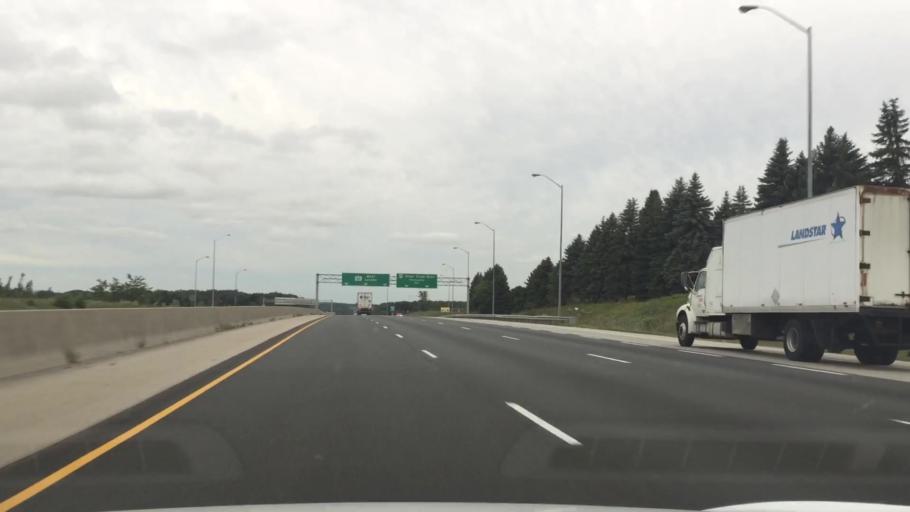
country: CA
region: Ontario
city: Kitchener
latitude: 43.3303
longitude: -80.4476
